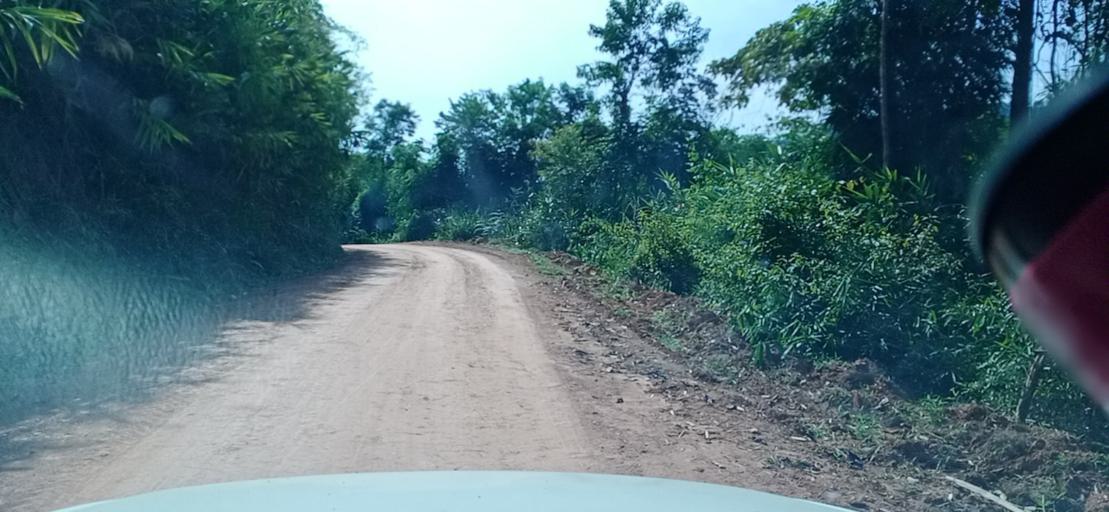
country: TH
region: Changwat Bueng Kan
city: Pak Khat
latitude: 18.6371
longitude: 103.2486
